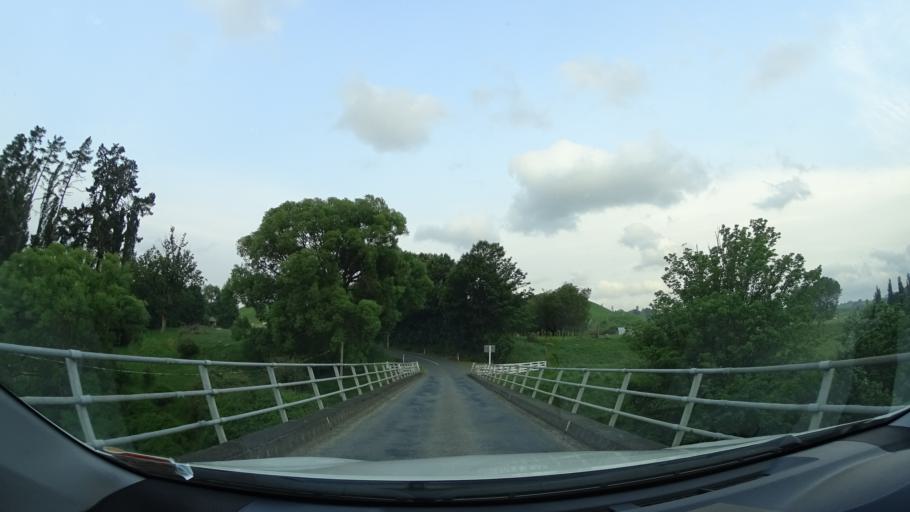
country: NZ
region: Manawatu-Wanganui
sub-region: Ruapehu District
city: Waiouru
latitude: -39.7189
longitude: 175.8416
